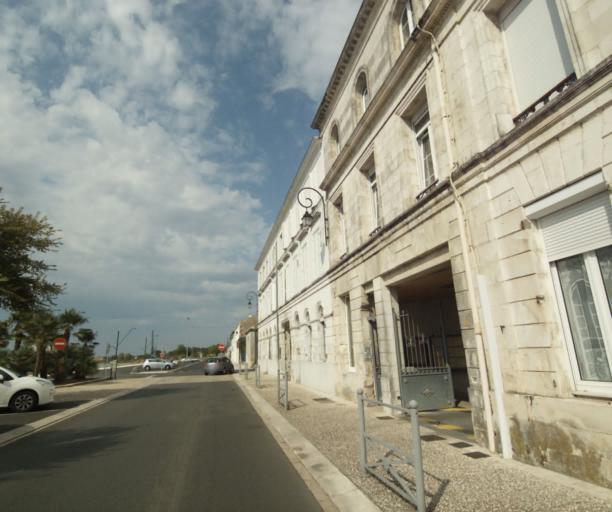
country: FR
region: Poitou-Charentes
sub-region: Departement de la Charente-Maritime
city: Tonnay-Charente
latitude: 45.9426
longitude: -0.8924
